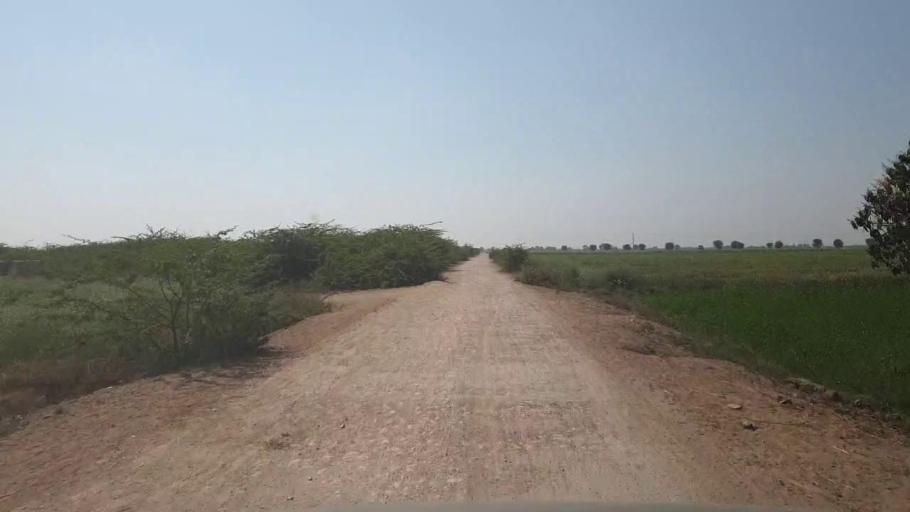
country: PK
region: Sindh
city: Digri
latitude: 25.2361
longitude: 69.2240
